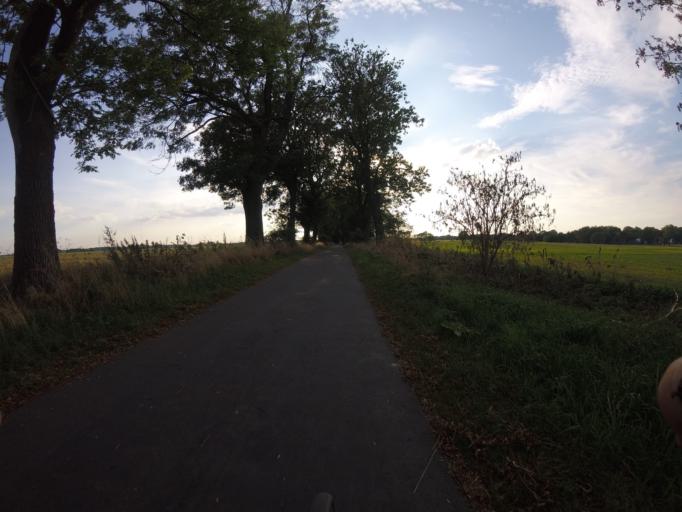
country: DE
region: Brandenburg
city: Altlandsberg
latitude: 52.5757
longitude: 13.6999
